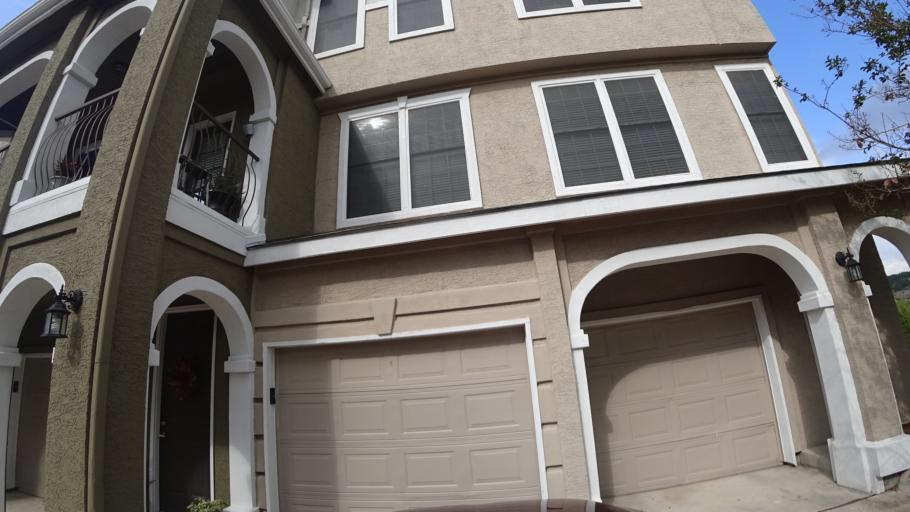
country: US
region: Texas
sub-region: Travis County
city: Hudson Bend
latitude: 30.3820
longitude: -97.8762
